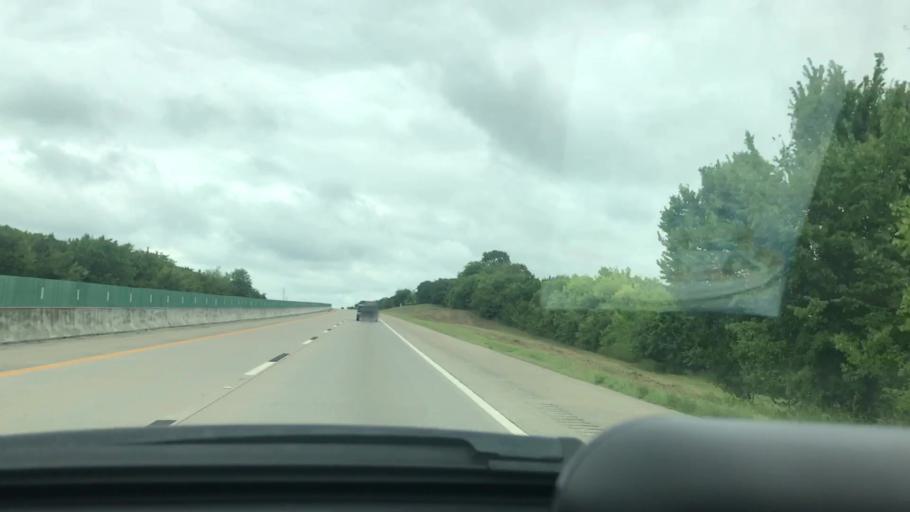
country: US
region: Oklahoma
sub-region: Pittsburg County
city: Krebs
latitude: 35.0312
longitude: -95.7138
